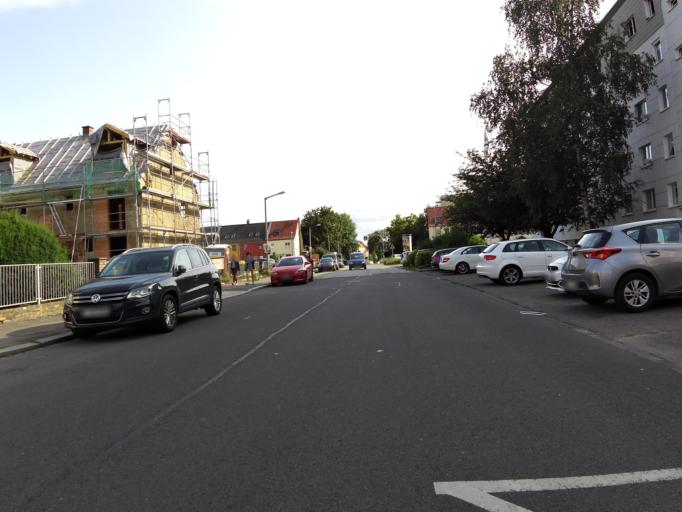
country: DE
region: Saxony
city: Leipzig
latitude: 51.3801
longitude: 12.4065
